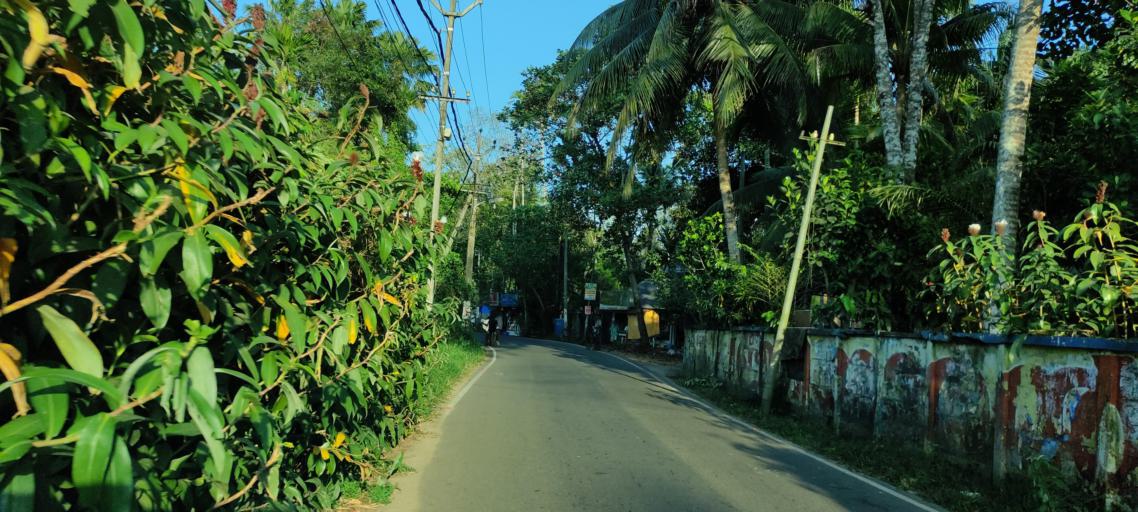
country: IN
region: Kerala
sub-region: Alappuzha
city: Shertallai
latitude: 9.6928
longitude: 76.3439
